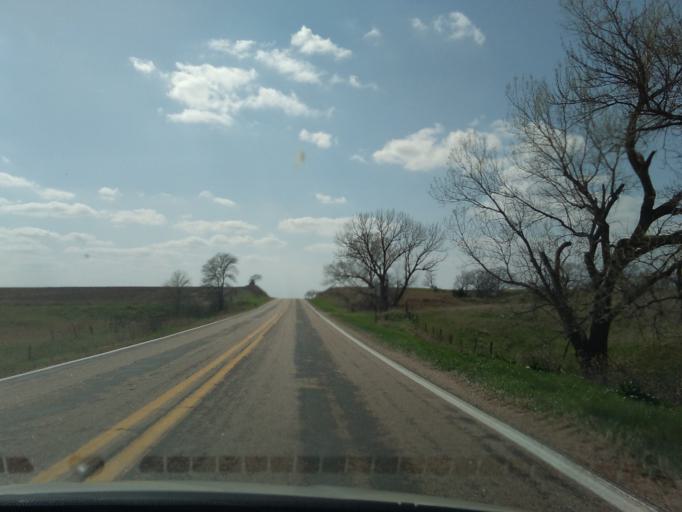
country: US
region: Nebraska
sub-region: Thayer County
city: Hebron
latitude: 40.1471
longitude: -97.6376
